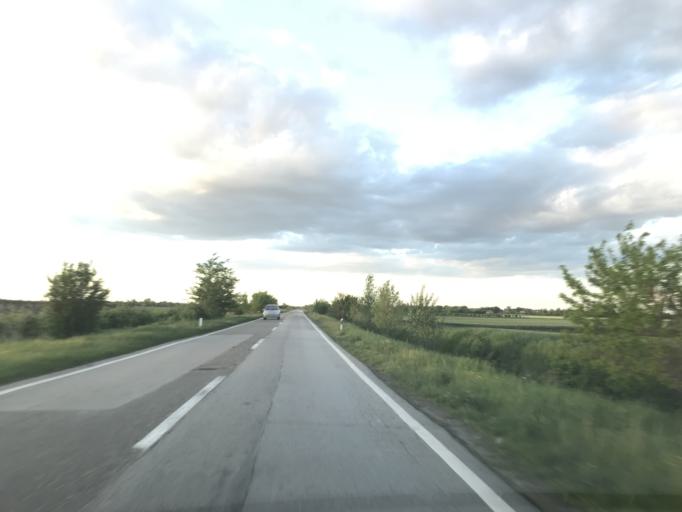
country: RS
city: Cestereg
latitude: 45.5762
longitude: 20.5449
